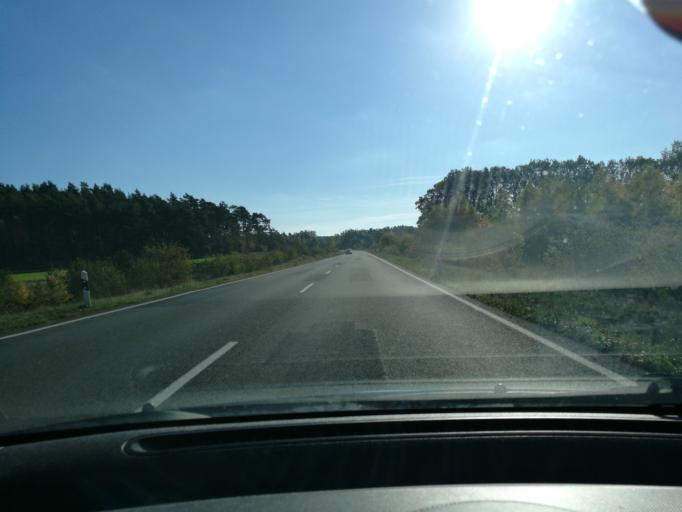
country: DE
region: Lower Saxony
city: Dahlem
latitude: 53.1836
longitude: 10.7633
